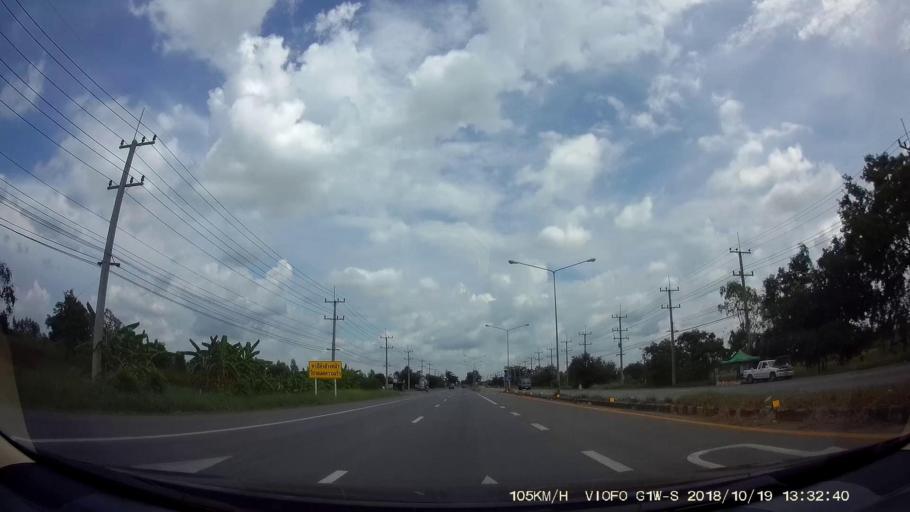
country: TH
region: Chaiyaphum
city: Chatturat
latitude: 15.5773
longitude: 101.8855
